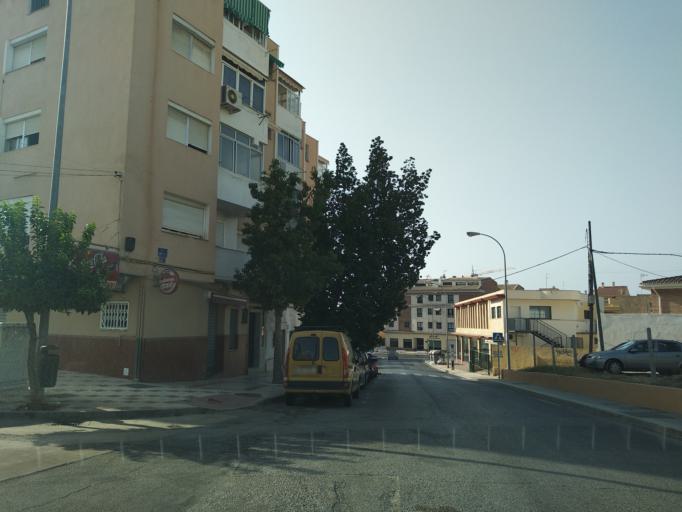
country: ES
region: Andalusia
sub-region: Provincia de Malaga
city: Malaga
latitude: 36.7238
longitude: -4.4516
